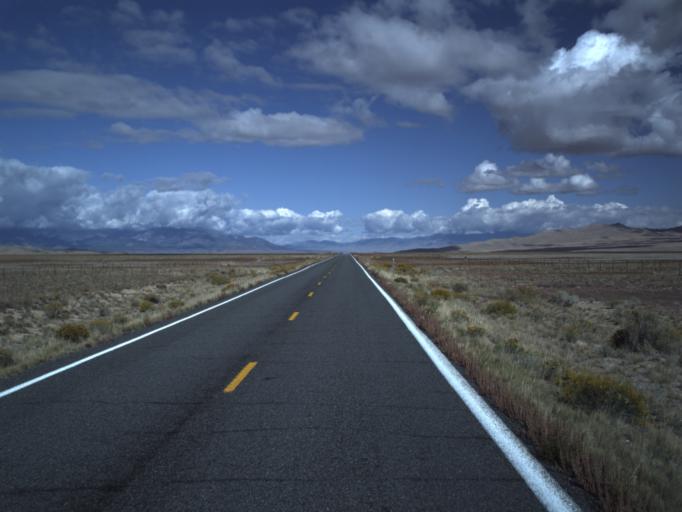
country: US
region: Utah
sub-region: Beaver County
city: Milford
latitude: 38.6465
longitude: -113.8660
